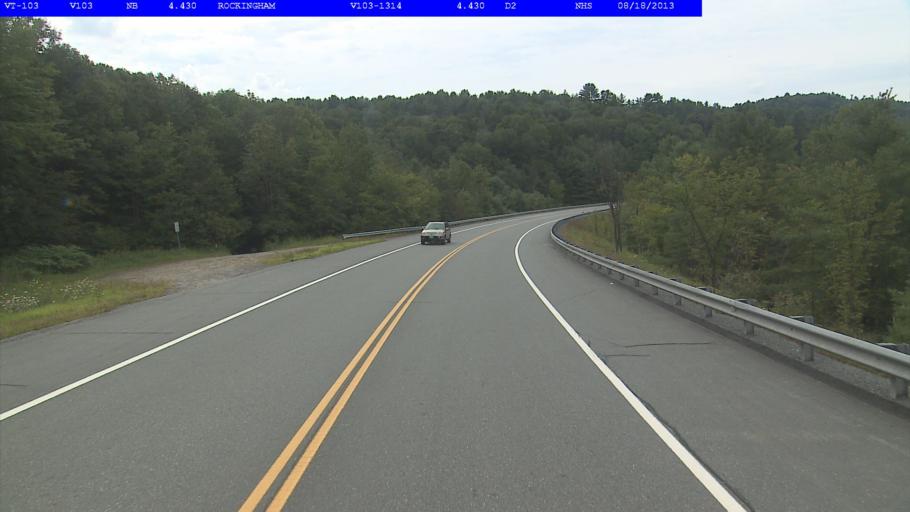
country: US
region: Vermont
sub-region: Windham County
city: Rockingham
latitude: 43.2062
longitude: -72.5353
